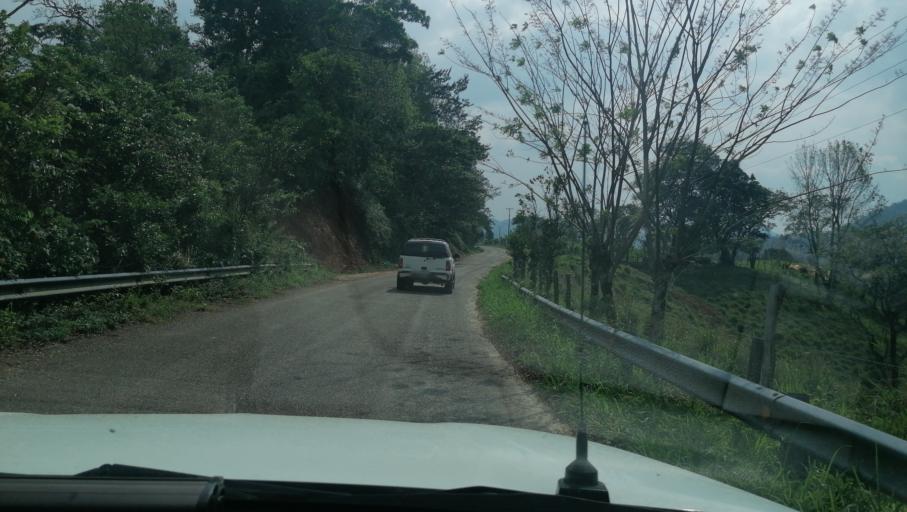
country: MX
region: Chiapas
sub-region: Francisco Leon
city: San Miguel la Sardina
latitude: 17.2323
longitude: -93.3422
